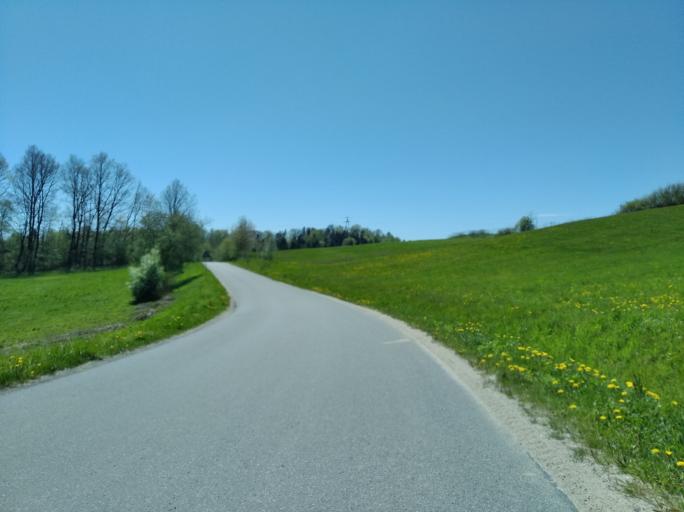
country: PL
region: Subcarpathian Voivodeship
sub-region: Powiat debicki
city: Brzostek
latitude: 49.9068
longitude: 21.4071
